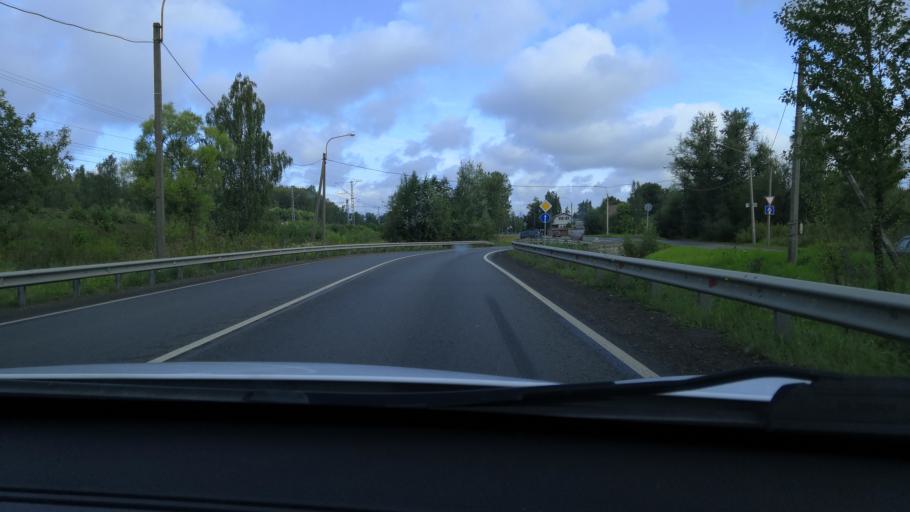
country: RU
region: St.-Petersburg
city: Tyarlevo
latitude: 59.7045
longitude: 30.4388
